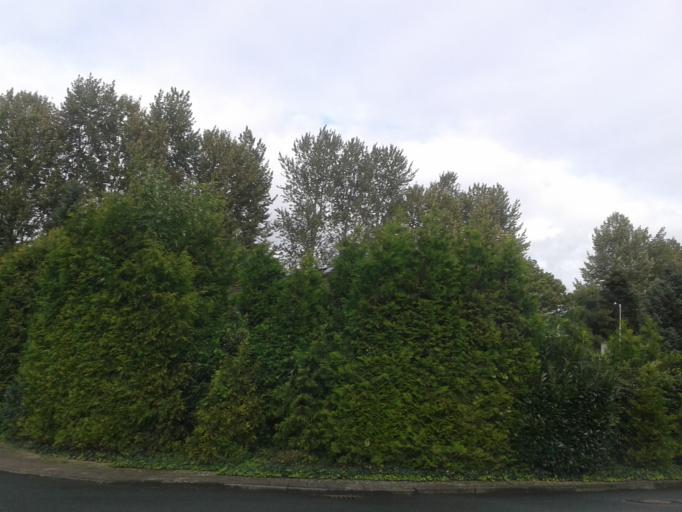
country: DE
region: North Rhine-Westphalia
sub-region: Regierungsbezirk Detmold
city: Hovelhof
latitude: 51.7634
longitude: 8.6667
